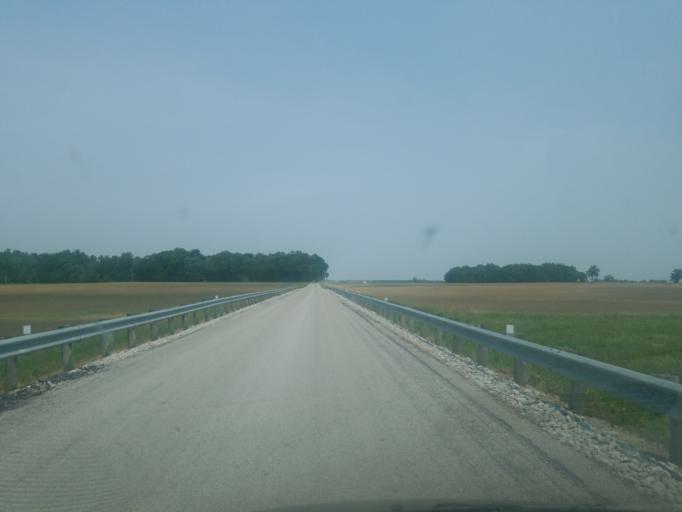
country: US
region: Ohio
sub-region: Marion County
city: Marion
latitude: 40.6994
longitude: -83.1114
